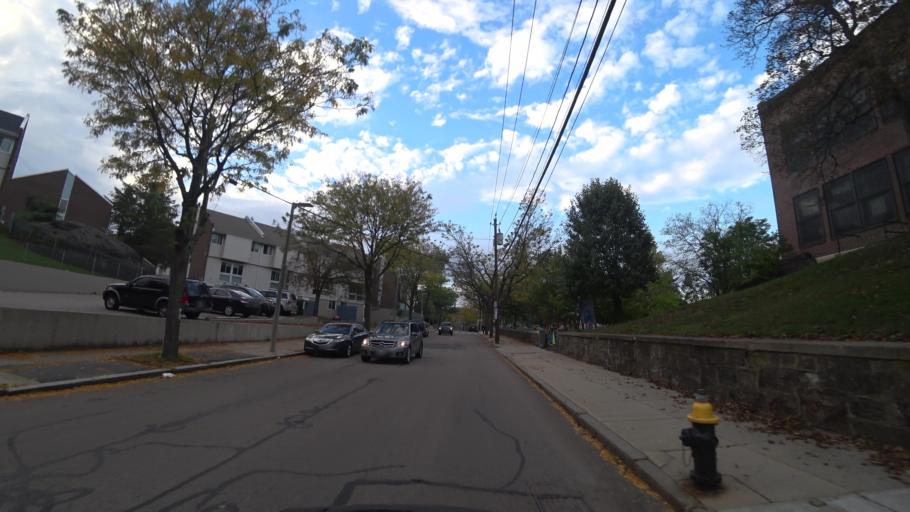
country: US
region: Massachusetts
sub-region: Norfolk County
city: Brookline
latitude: 42.3253
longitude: -71.0913
